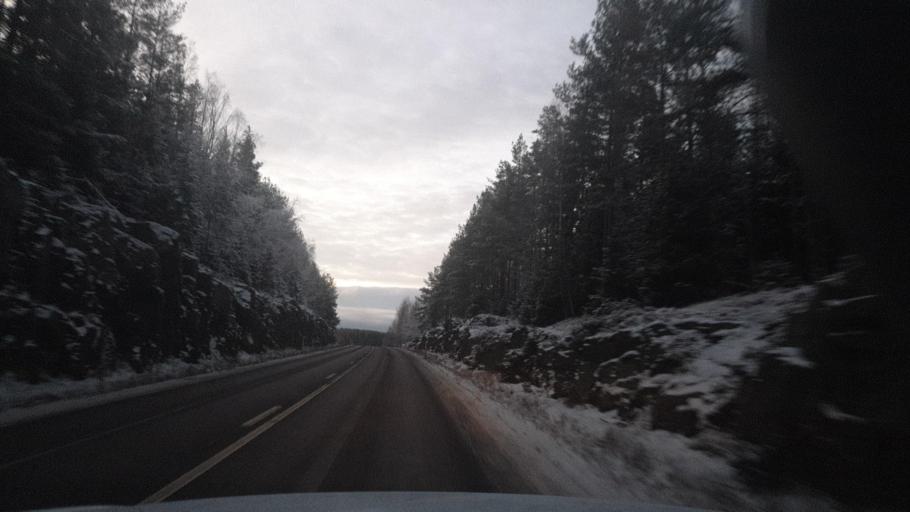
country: SE
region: Vaermland
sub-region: Arvika Kommun
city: Arvika
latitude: 59.4909
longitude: 12.7606
